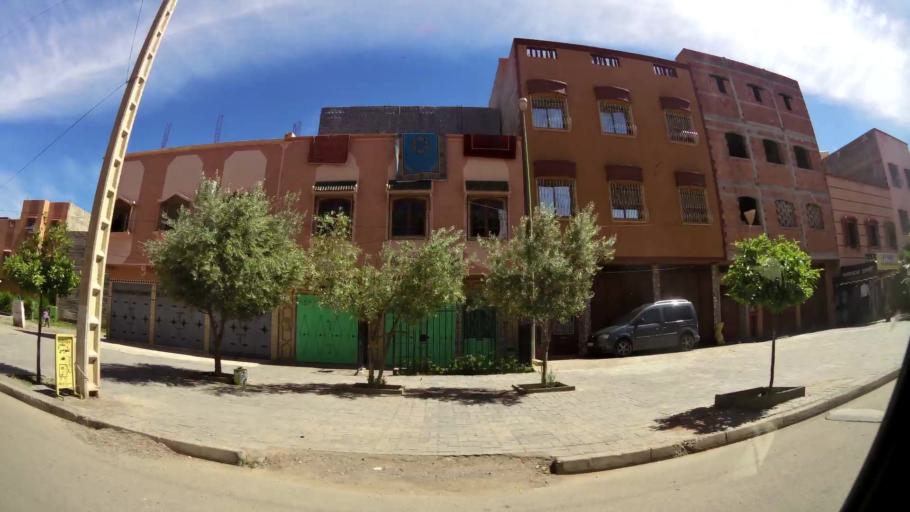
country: MA
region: Marrakech-Tensift-Al Haouz
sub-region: Marrakech
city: Marrakesh
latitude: 31.5970
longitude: -7.9591
